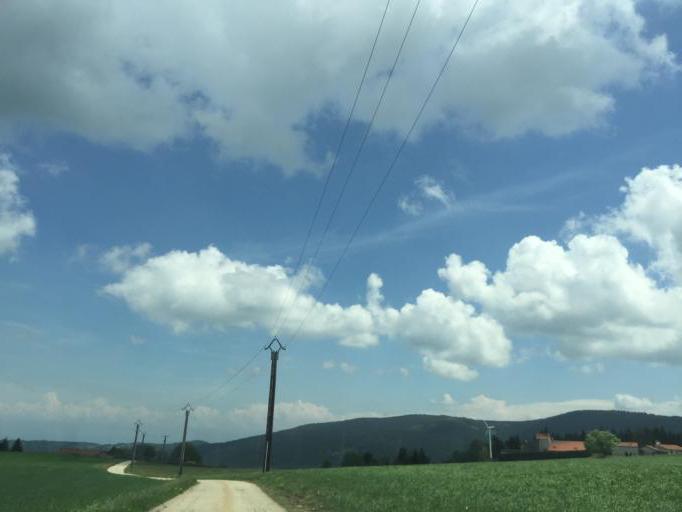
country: FR
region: Rhone-Alpes
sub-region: Departement de la Loire
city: Saint-Sauveur-en-Rue
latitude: 45.2697
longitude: 4.4648
